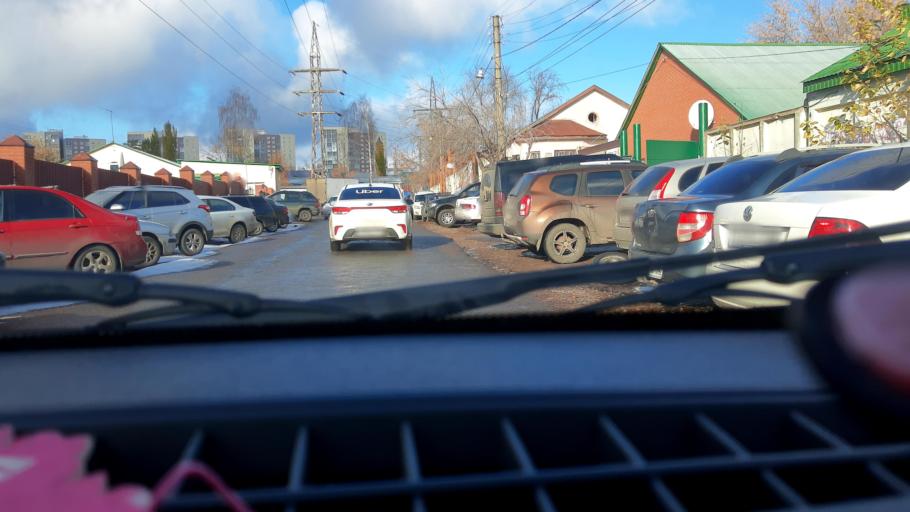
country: RU
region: Bashkortostan
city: Ufa
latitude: 54.7540
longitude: 56.0171
